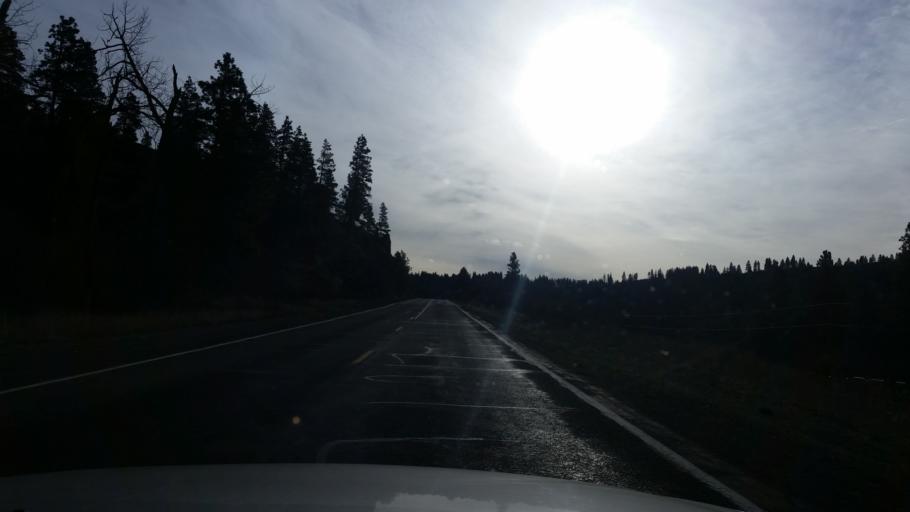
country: US
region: Washington
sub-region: Kittitas County
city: Cle Elum
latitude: 47.1387
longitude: -120.7921
